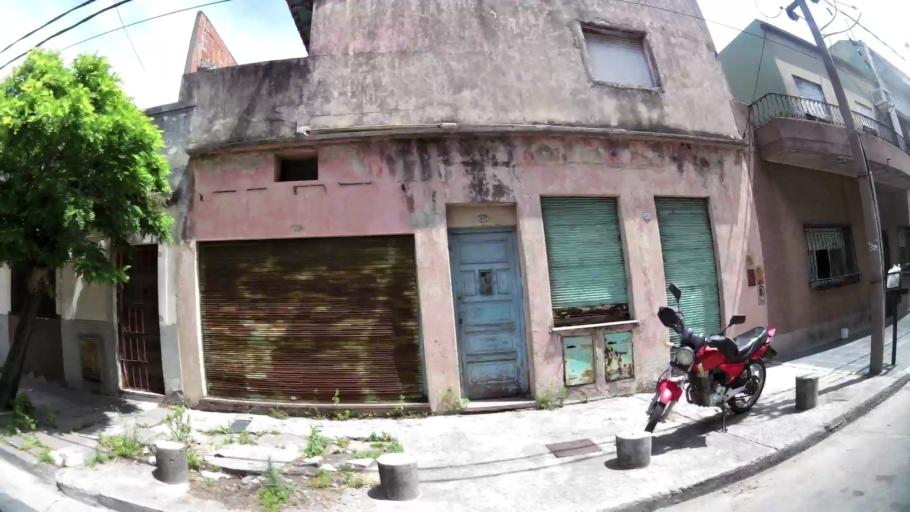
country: AR
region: Buenos Aires
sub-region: Partido de Lanus
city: Lanus
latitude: -34.6667
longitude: -58.4104
